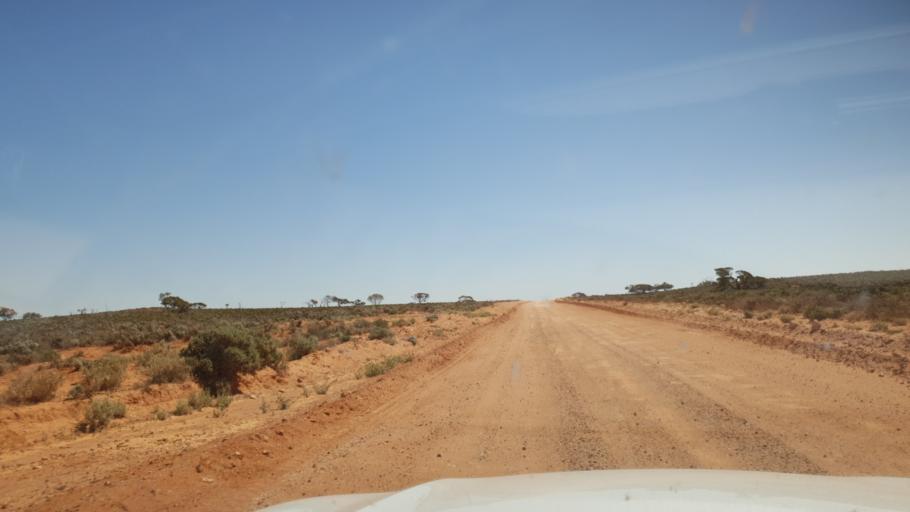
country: AU
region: South Australia
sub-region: Whyalla
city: Whyalla
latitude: -32.6511
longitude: 136.9851
